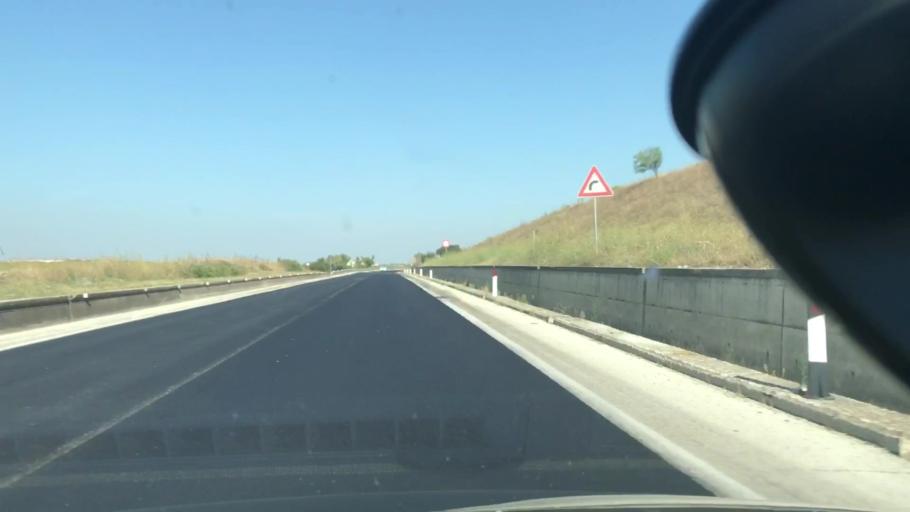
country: IT
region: Apulia
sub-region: Provincia di Barletta - Andria - Trani
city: Spinazzola
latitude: 40.9063
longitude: 16.1114
